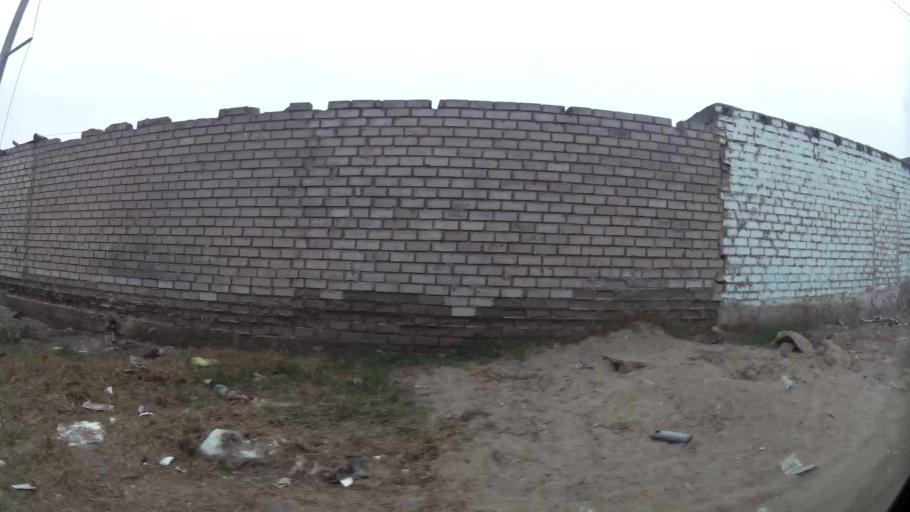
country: PE
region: Lima
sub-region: Lima
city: Surco
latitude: -12.2026
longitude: -76.9865
